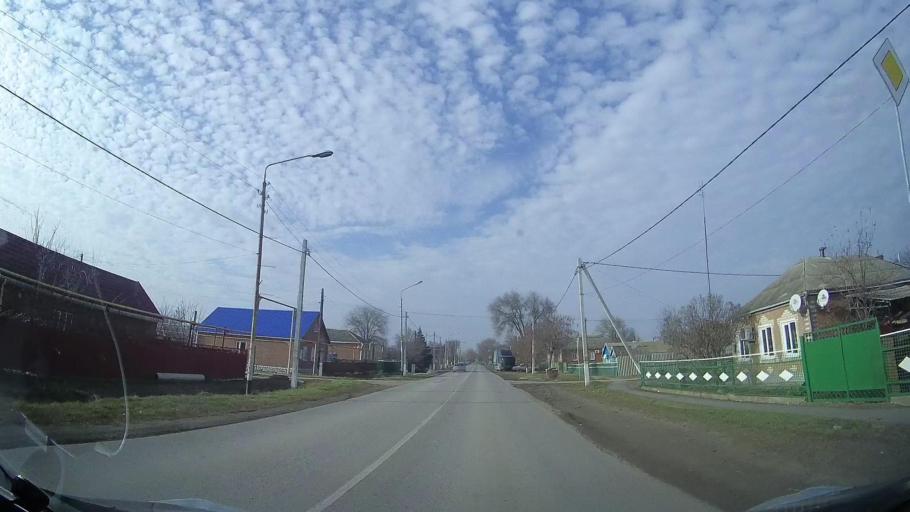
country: RU
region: Rostov
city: Veselyy
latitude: 47.0888
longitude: 40.7515
